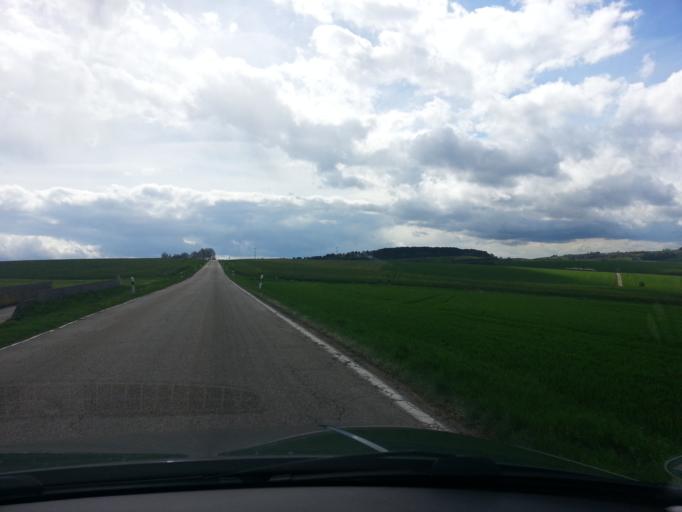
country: DE
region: Rheinland-Pfalz
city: Massweiler
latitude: 49.2762
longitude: 7.5256
